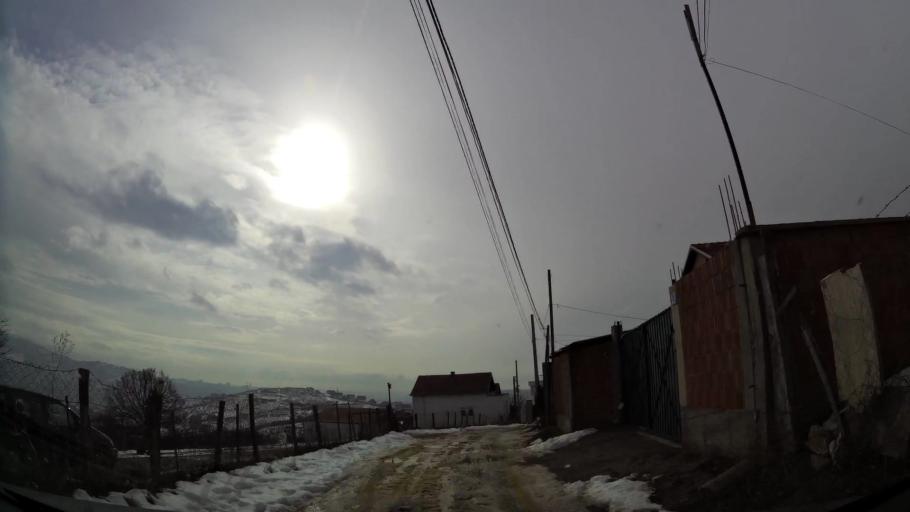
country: XK
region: Pristina
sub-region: Komuna e Prishtines
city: Pristina
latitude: 42.6922
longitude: 21.1695
